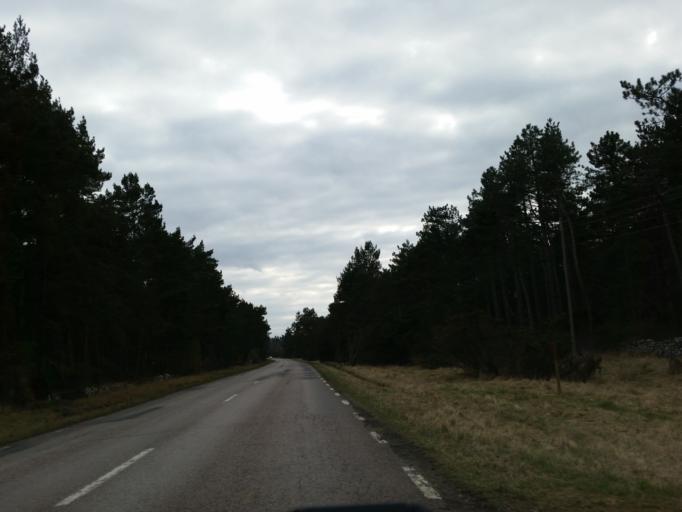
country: SE
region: Kalmar
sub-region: Morbylanga Kommun
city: Sodra Sandby
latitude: 56.5829
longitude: 16.6229
